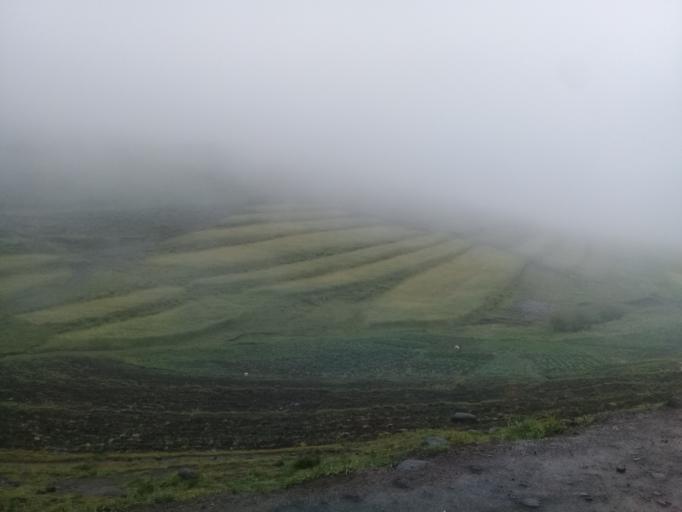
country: LS
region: Mokhotlong
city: Mokhotlong
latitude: -29.3873
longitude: 28.9751
